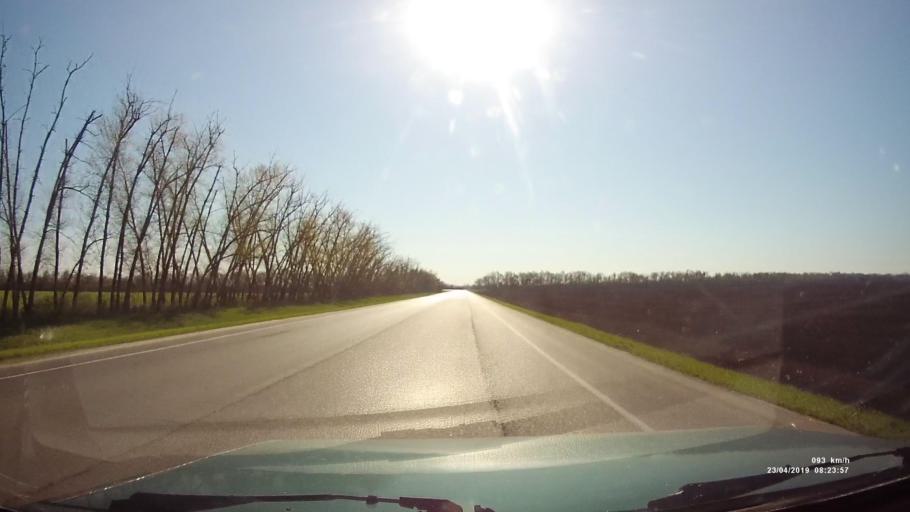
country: RU
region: Rostov
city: Tselina
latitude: 46.5320
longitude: 40.9401
